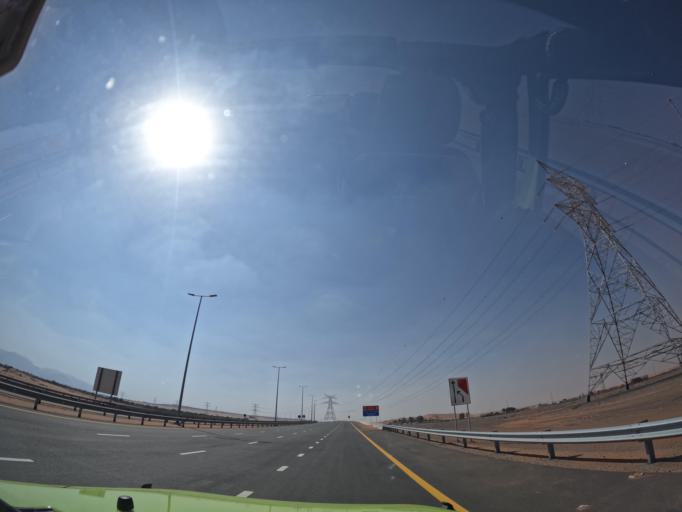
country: AE
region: Ash Shariqah
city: Adh Dhayd
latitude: 24.8073
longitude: 55.8010
